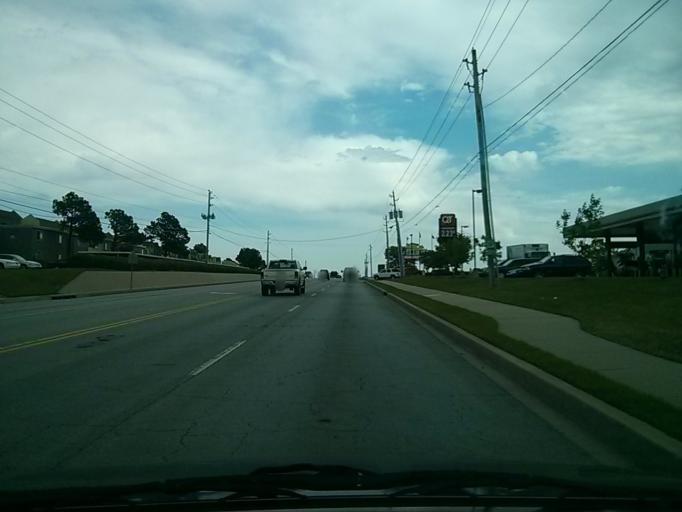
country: US
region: Oklahoma
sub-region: Tulsa County
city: Jenks
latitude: 36.0754
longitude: -95.8913
